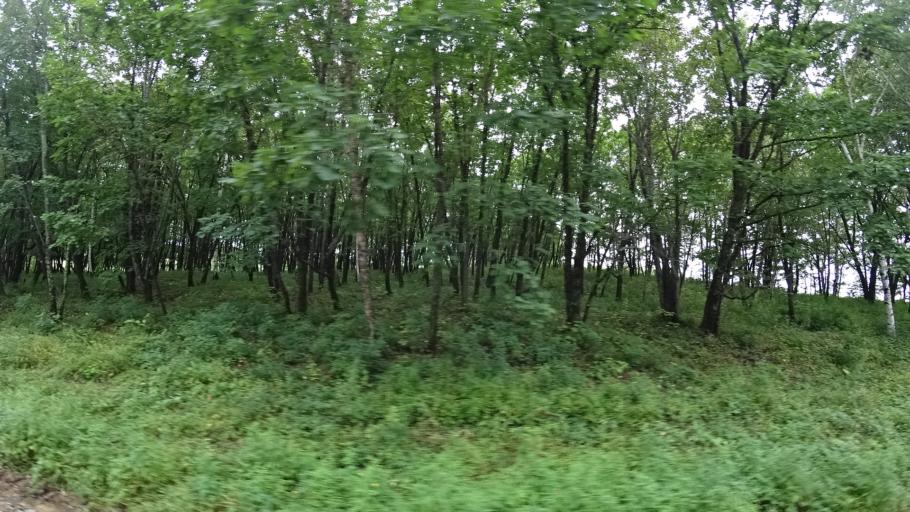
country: RU
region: Primorskiy
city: Rettikhovka
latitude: 44.0665
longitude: 132.6478
